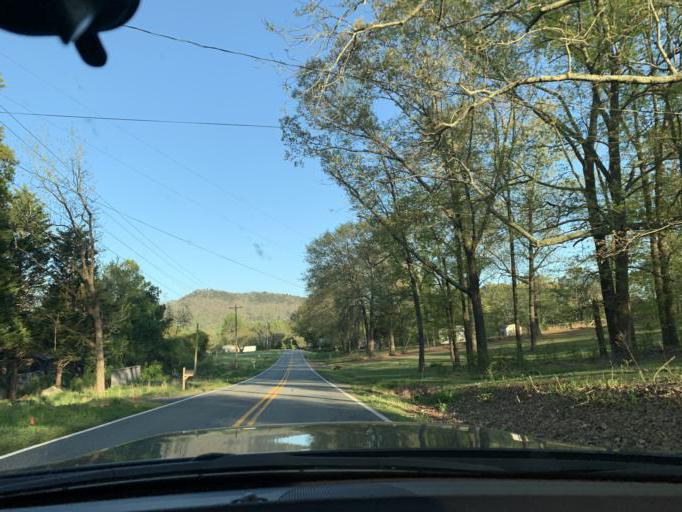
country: US
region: Georgia
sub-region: Forsyth County
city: Cumming
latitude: 34.2435
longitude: -84.1831
